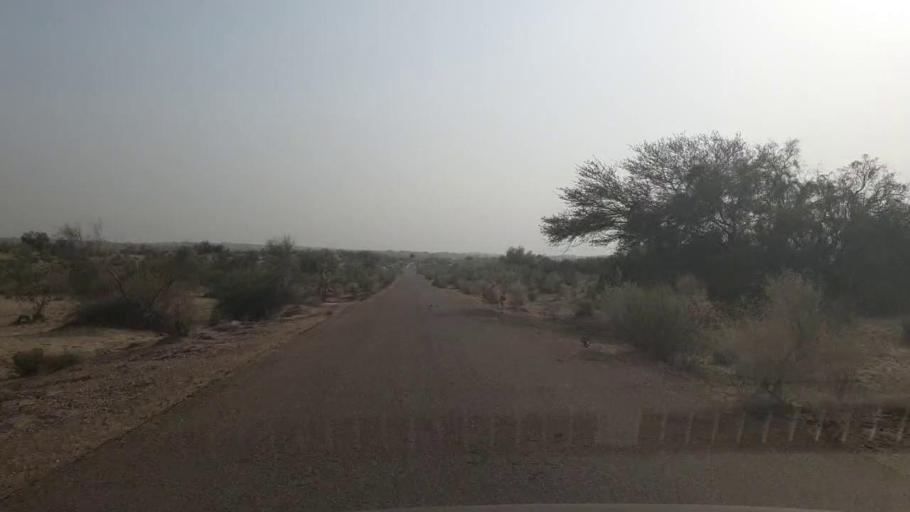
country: PK
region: Sindh
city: Chor
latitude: 25.4782
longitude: 69.9736
